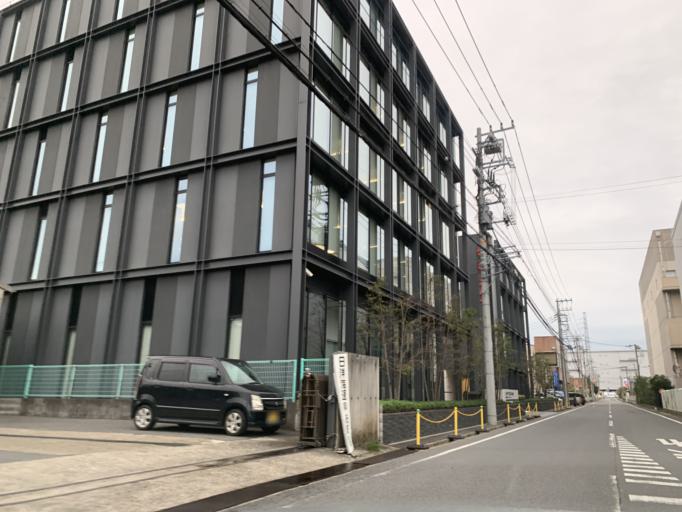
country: JP
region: Chiba
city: Kashiwa
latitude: 35.9046
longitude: 139.9400
